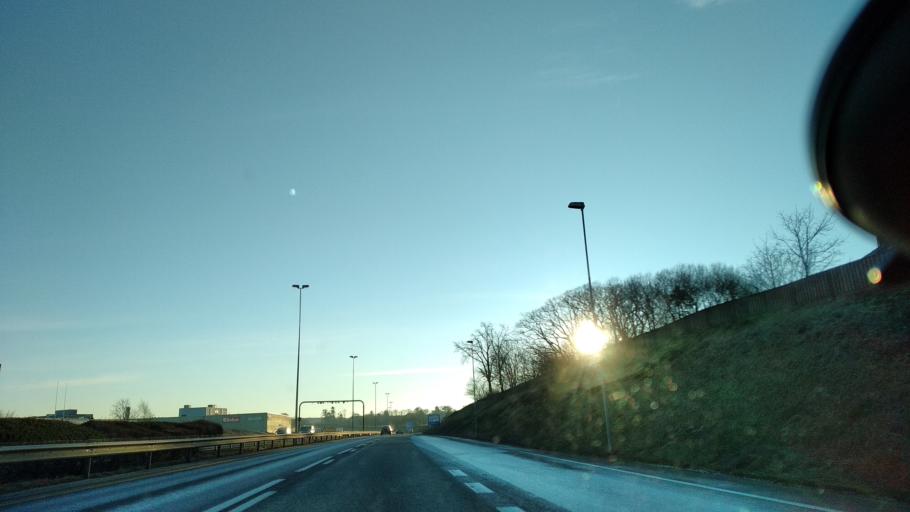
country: NO
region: Rogaland
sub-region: Sandnes
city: Sandnes
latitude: 58.8836
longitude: 5.7180
